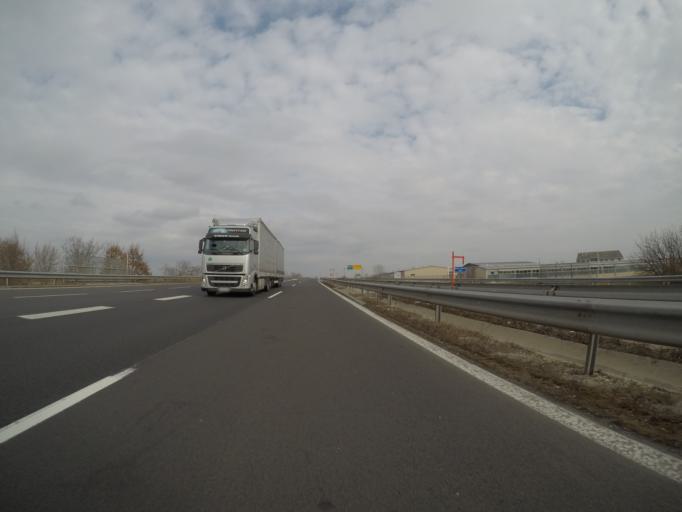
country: SI
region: Murska Sobota
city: Krog
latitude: 46.6336
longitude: 16.1539
